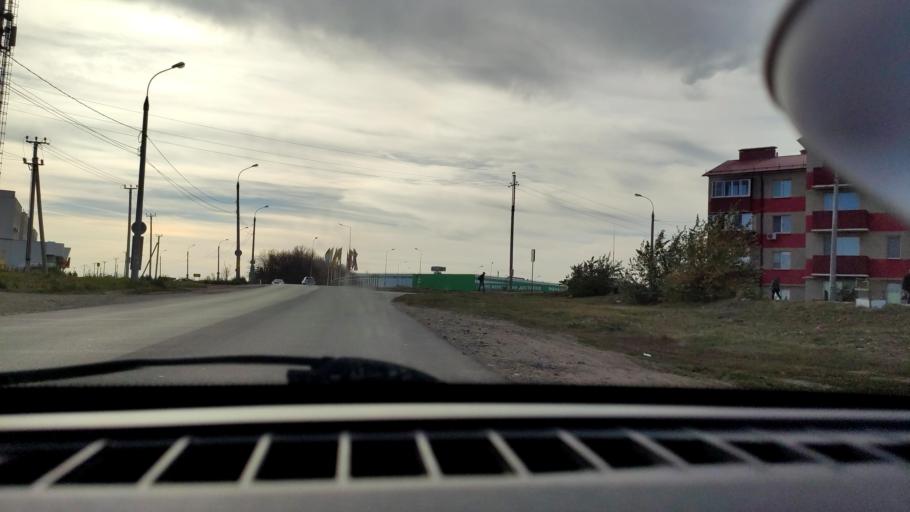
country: RU
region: Samara
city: Novosemeykino
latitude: 53.3291
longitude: 50.3126
